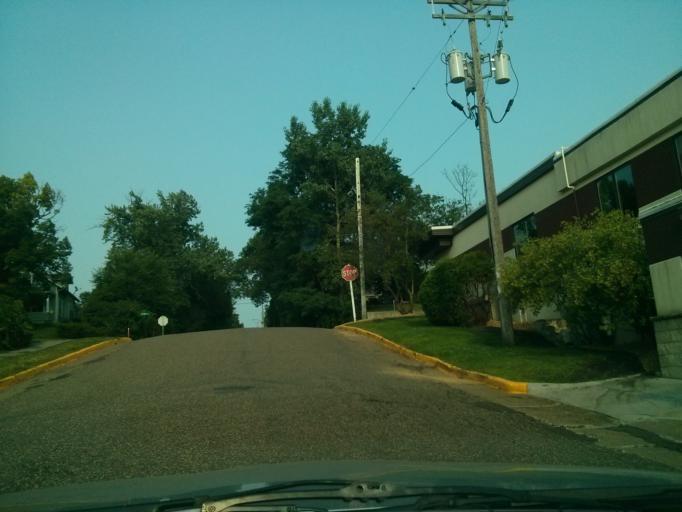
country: US
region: Wisconsin
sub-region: Saint Croix County
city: Hudson
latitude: 44.9781
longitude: -92.7576
